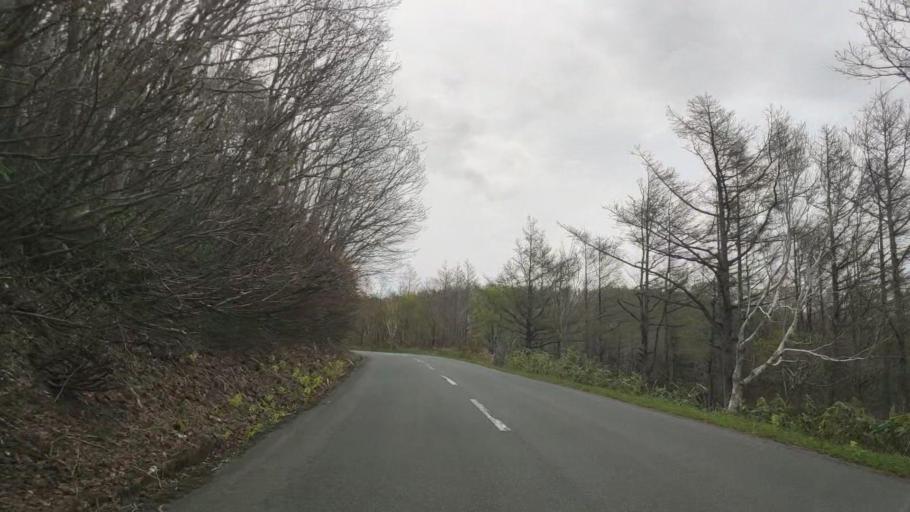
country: JP
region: Aomori
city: Aomori Shi
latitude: 40.7155
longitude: 140.8684
